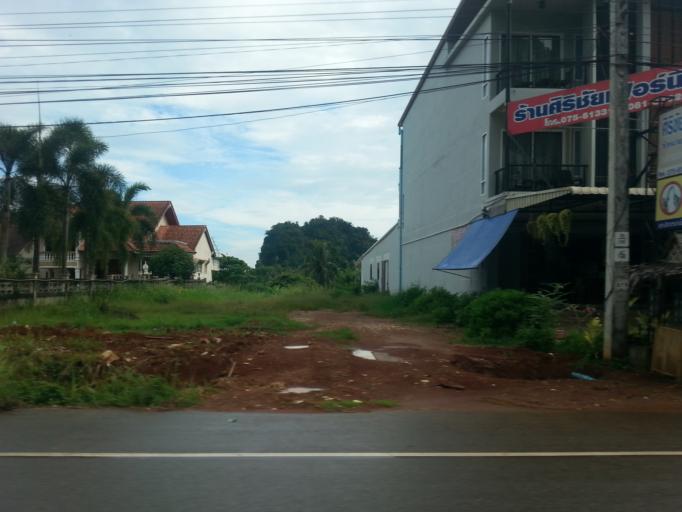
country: TH
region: Krabi
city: Krabi
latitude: 8.0857
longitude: 98.8749
